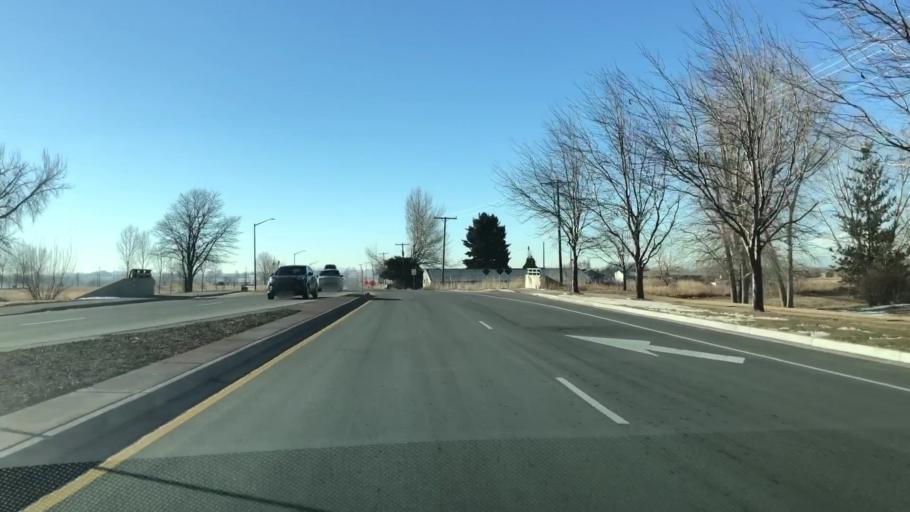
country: US
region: Colorado
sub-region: Larimer County
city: Loveland
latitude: 40.4045
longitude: -105.0211
